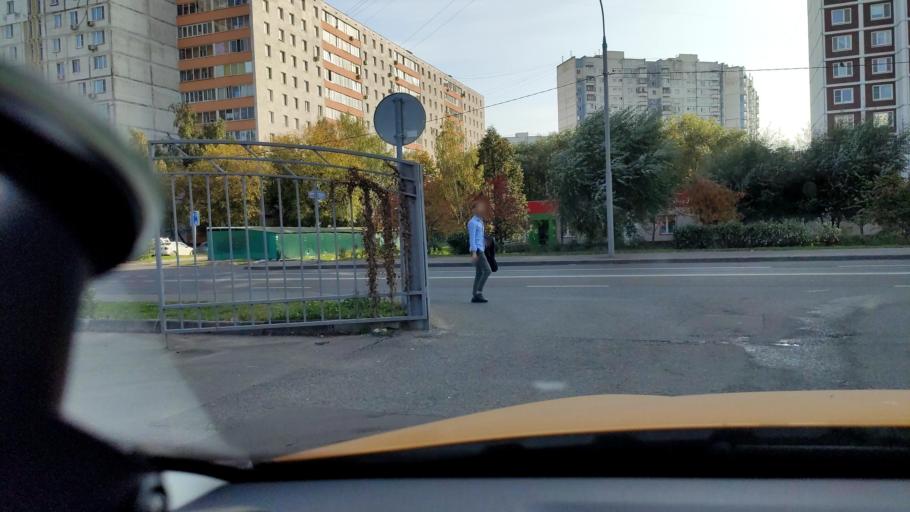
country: RU
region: Moscow
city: Altuf'yevskiy
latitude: 55.8874
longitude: 37.5901
